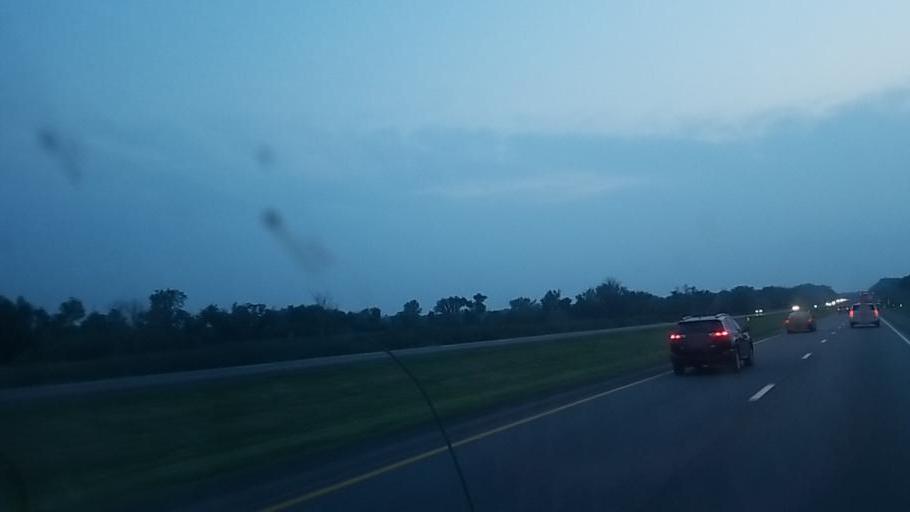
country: US
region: New York
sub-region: Madison County
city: Bolivar
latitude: 43.0959
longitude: -75.8514
